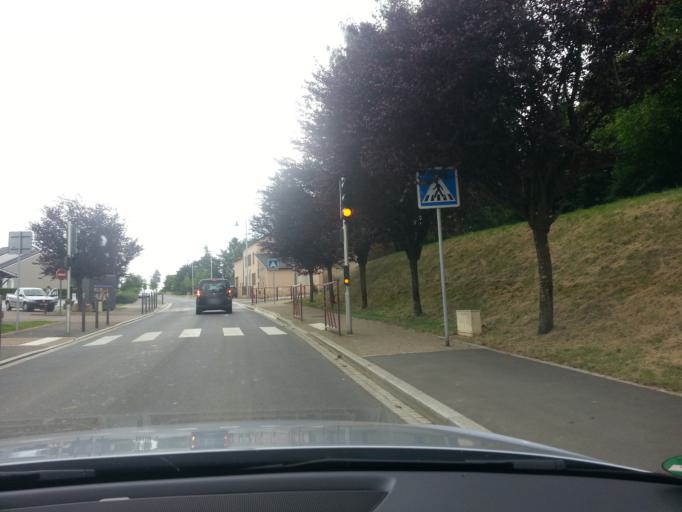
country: LU
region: Grevenmacher
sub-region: Canton de Remich
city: Mondorf-les-Bains
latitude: 49.5031
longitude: 6.2715
